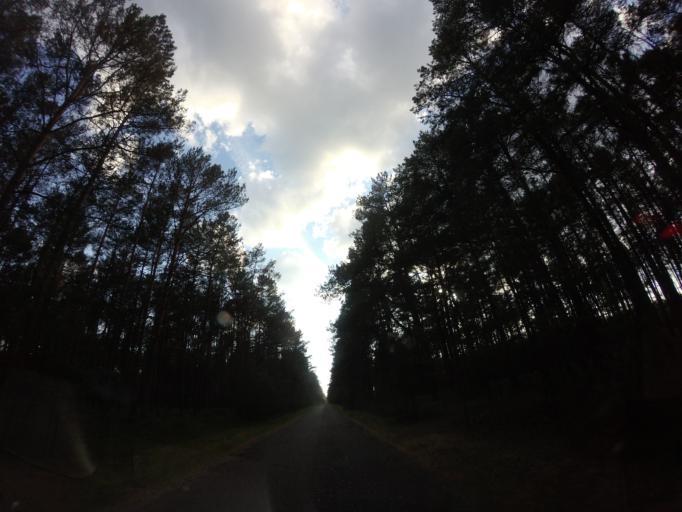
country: PL
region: West Pomeranian Voivodeship
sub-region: Powiat drawski
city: Kalisz Pomorski
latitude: 53.2003
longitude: 15.9161
